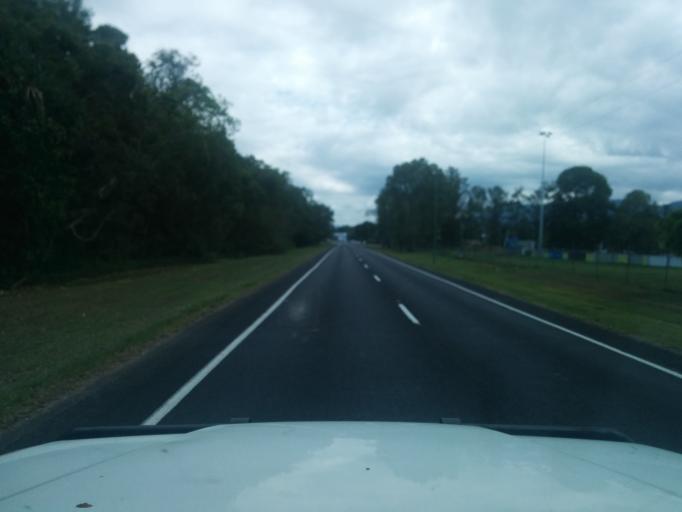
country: AU
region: Queensland
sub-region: Cairns
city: Cairns
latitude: -16.9074
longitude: 145.7504
